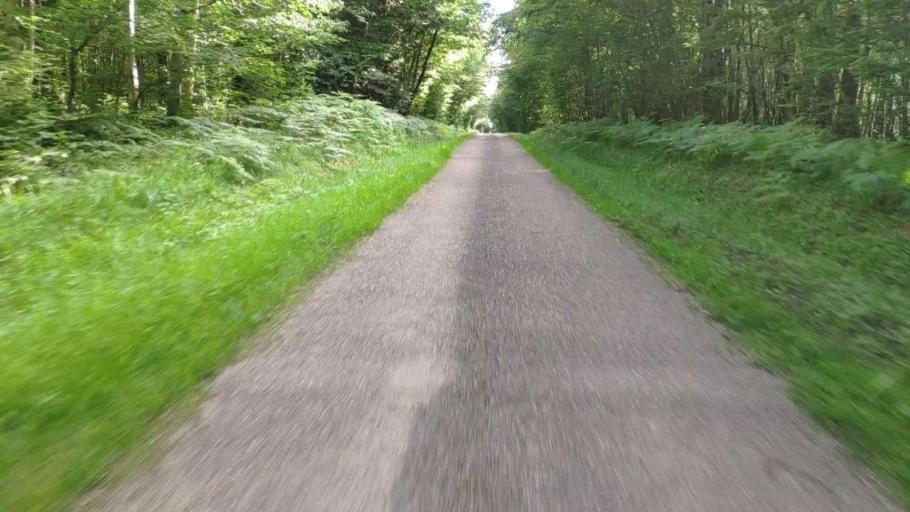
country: FR
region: Franche-Comte
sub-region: Departement du Jura
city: Bletterans
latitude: 46.8188
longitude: 5.5208
